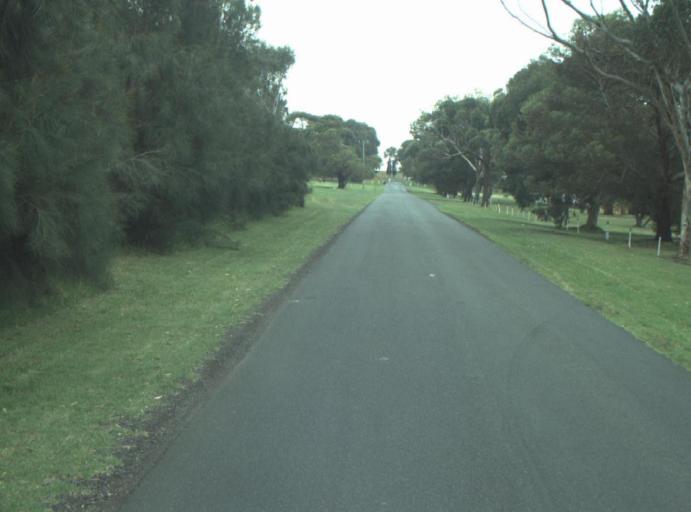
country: AU
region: Victoria
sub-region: Greater Geelong
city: East Geelong
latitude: -38.1527
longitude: 144.3849
